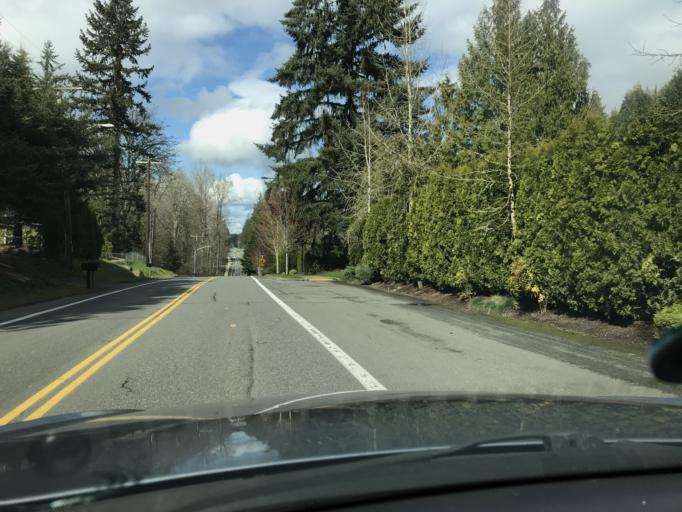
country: US
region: Washington
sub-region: King County
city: City of Sammamish
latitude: 47.5862
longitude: -122.0568
